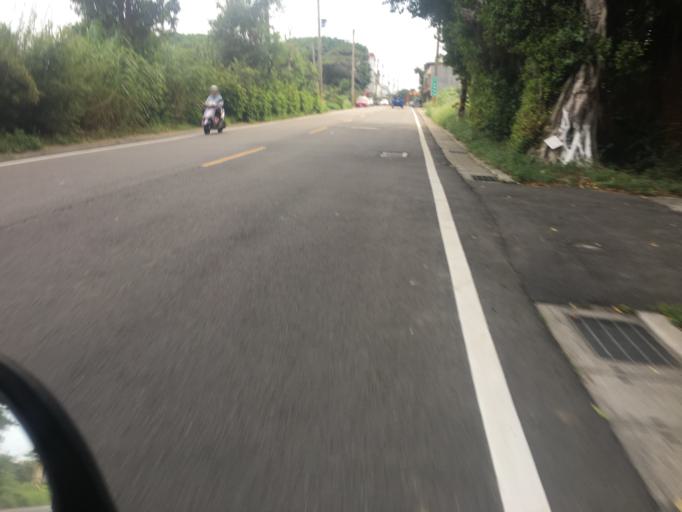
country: TW
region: Taiwan
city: Taoyuan City
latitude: 25.0966
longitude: 121.2358
